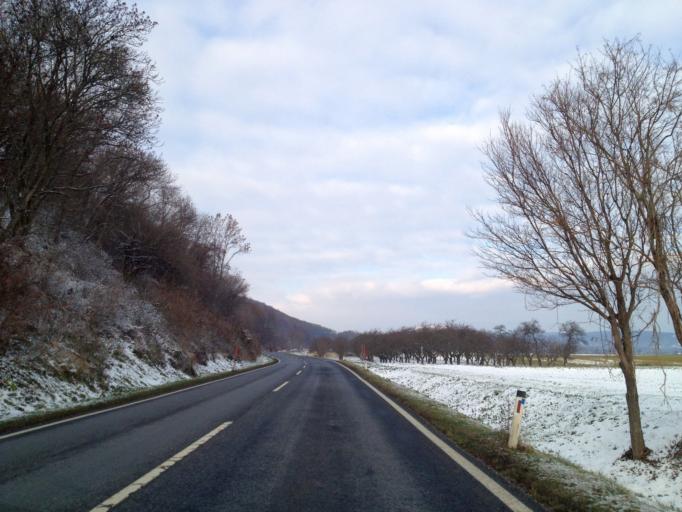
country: AT
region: Lower Austria
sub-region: Politischer Bezirk Bruck an der Leitha
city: Berg
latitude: 48.1086
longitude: 17.0414
